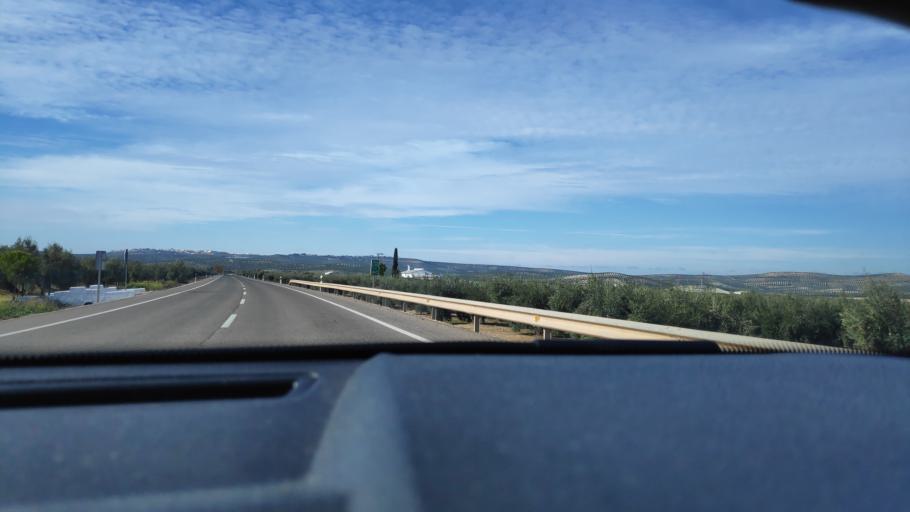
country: ES
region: Andalusia
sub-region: Provincia de Jaen
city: Higuera de Calatrava
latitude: 37.8417
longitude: -4.1113
